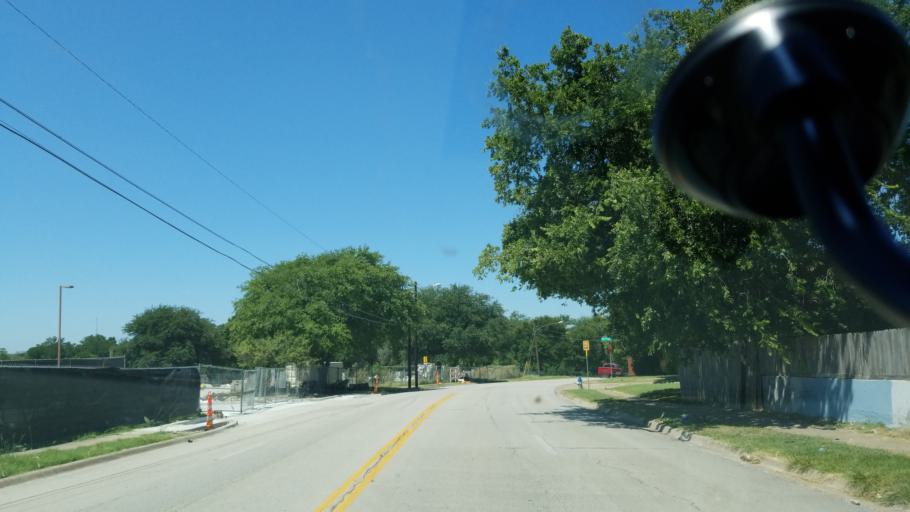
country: US
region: Texas
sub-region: Dallas County
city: Cockrell Hill
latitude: 32.7005
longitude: -96.8166
